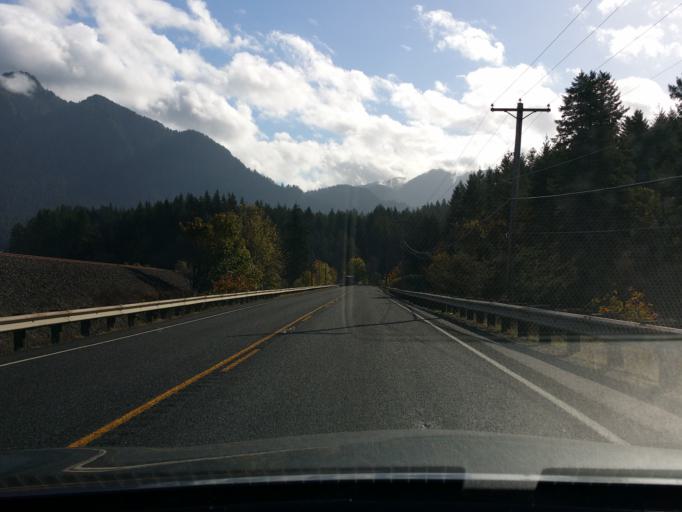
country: US
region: Oregon
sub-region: Hood River County
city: Cascade Locks
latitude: 45.6731
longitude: -121.9097
